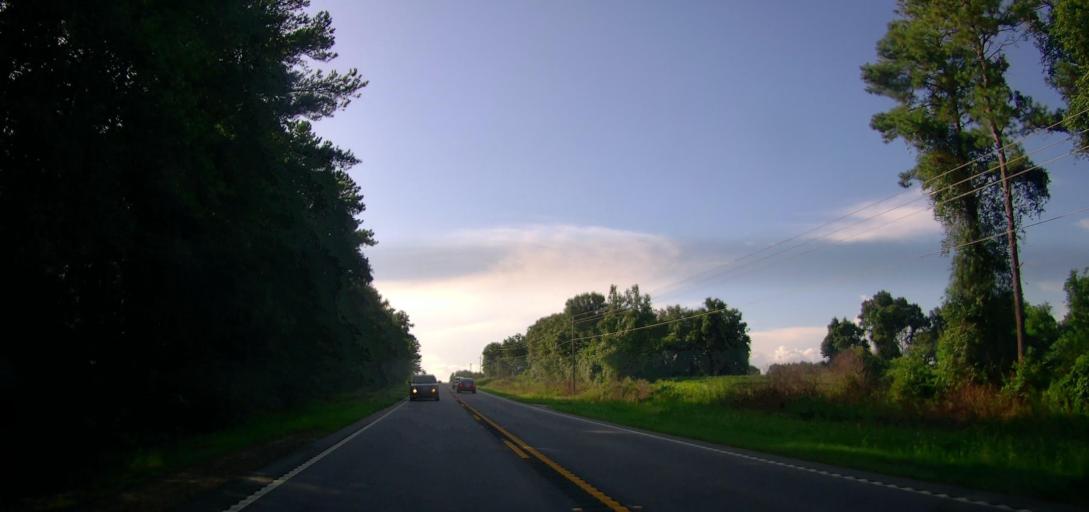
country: US
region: Georgia
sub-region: Coffee County
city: Nicholls
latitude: 31.3954
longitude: -82.6655
